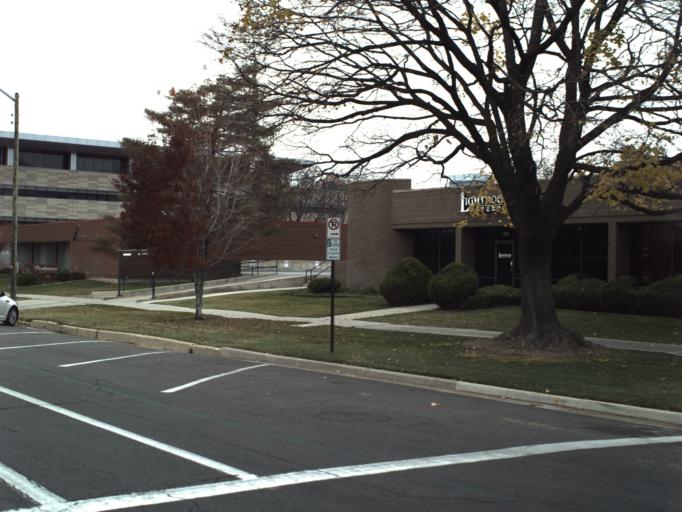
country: US
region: Utah
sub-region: Salt Lake County
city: Salt Lake City
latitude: 40.7585
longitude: -111.8798
